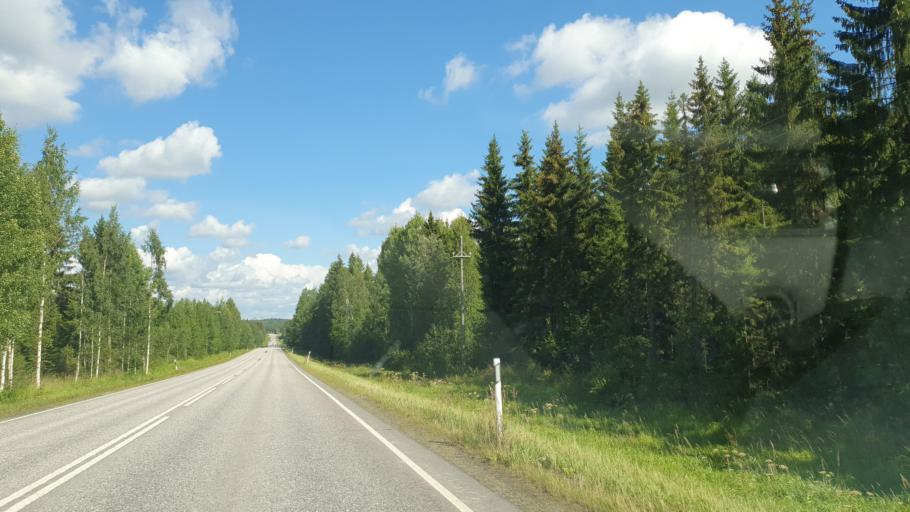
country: FI
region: Northern Savo
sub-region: Ylae-Savo
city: Sonkajaervi
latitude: 63.7157
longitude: 27.3636
